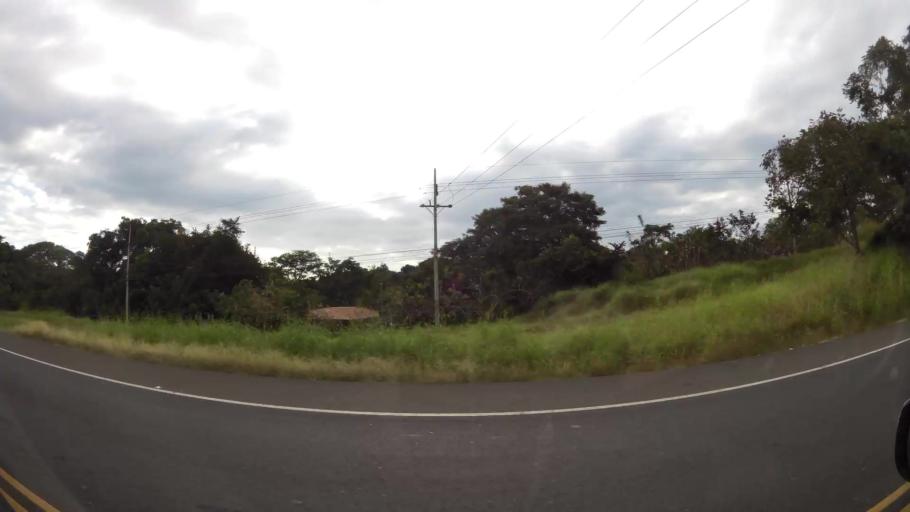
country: CR
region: Puntarenas
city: Esparza
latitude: 9.9023
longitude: -84.6595
